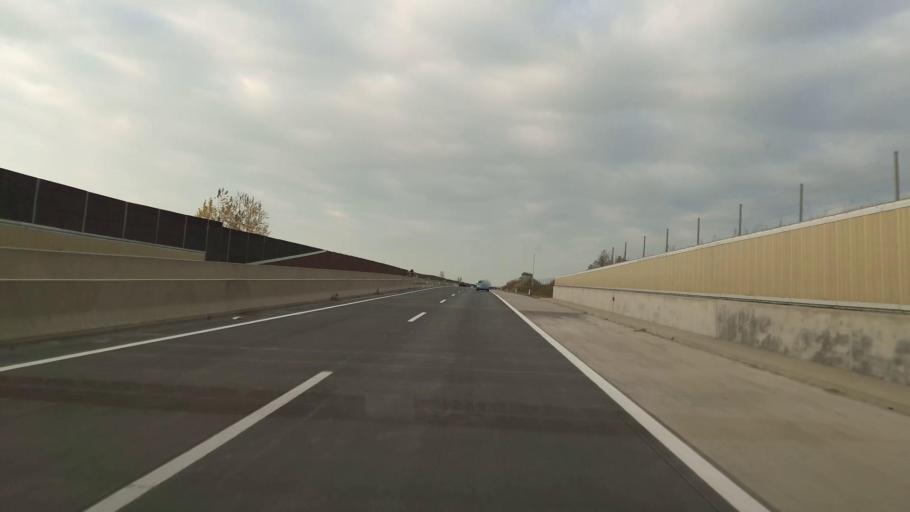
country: AT
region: Lower Austria
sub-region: Politischer Bezirk Ganserndorf
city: Aderklaa
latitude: 48.2931
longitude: 16.5129
